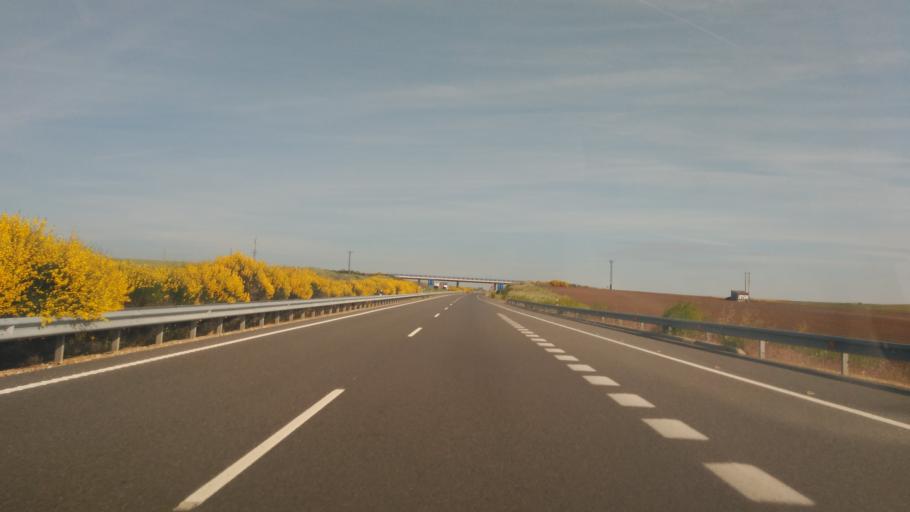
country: ES
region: Castille and Leon
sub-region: Provincia de Salamanca
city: Calzada de Valdunciel
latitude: 41.0912
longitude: -5.6927
